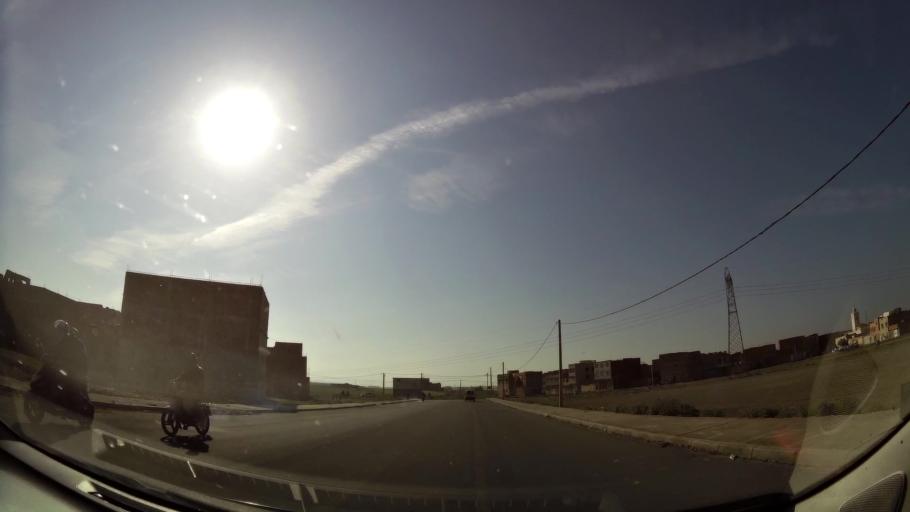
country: MA
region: Oriental
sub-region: Oujda-Angad
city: Oujda
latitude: 34.7214
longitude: -1.8909
